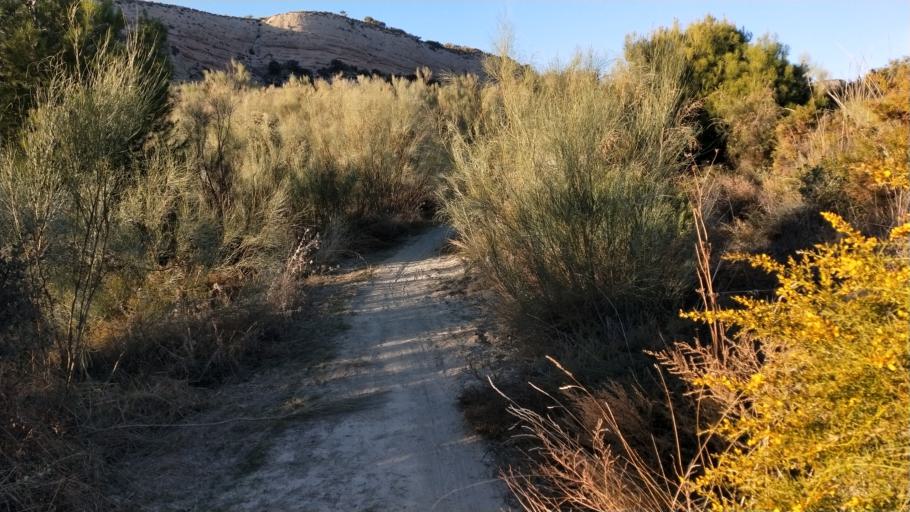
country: ES
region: Andalusia
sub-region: Provincia de Granada
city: Dudar
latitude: 37.1961
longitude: -3.5010
